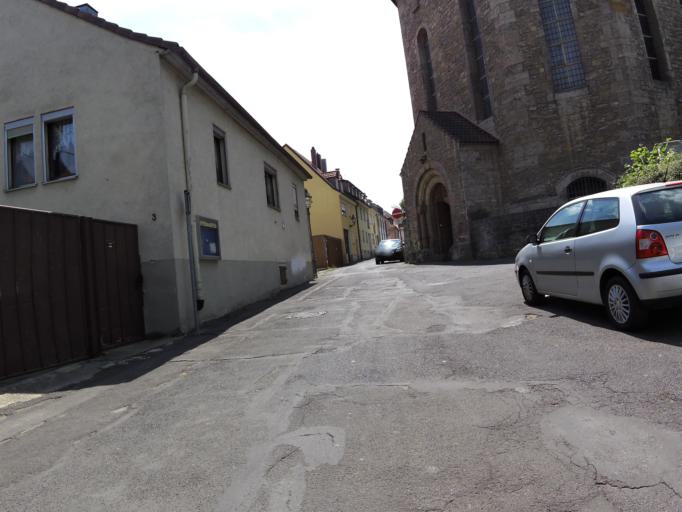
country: DE
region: Bavaria
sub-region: Regierungsbezirk Unterfranken
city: Wuerzburg
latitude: 49.7633
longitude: 9.9523
